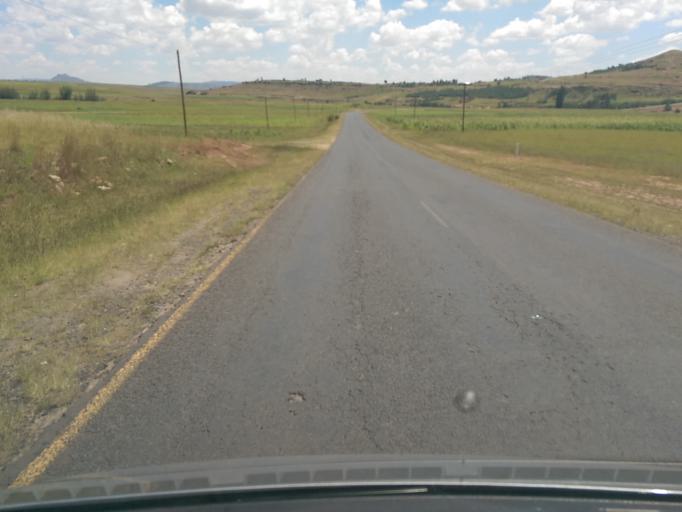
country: LS
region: Maseru
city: Nako
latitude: -29.4372
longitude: 27.6978
